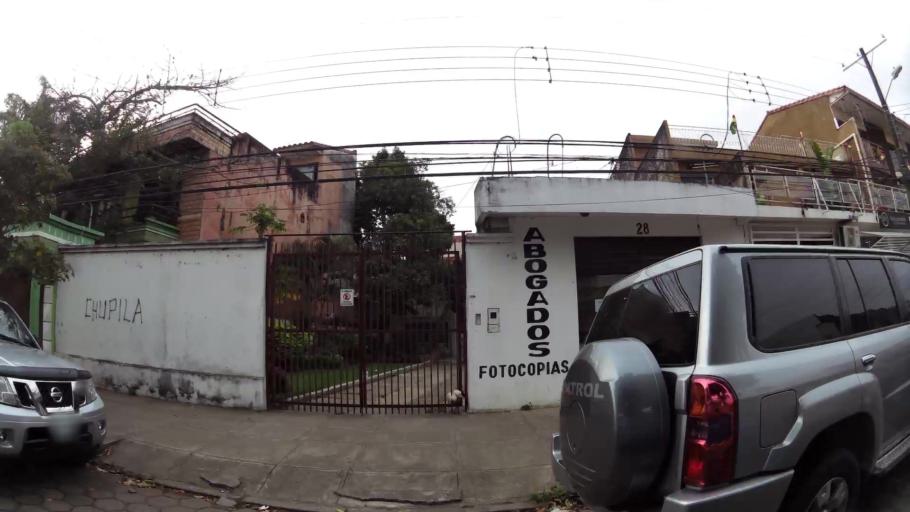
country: BO
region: Santa Cruz
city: Santa Cruz de la Sierra
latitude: -17.7884
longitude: -63.1886
